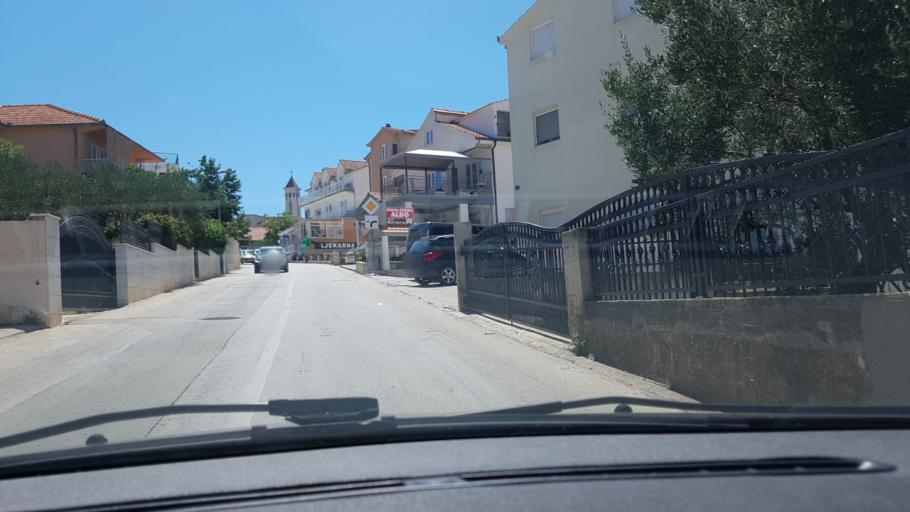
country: HR
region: Splitsko-Dalmatinska
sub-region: Grad Trogir
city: Trogir
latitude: 43.4944
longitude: 16.2636
